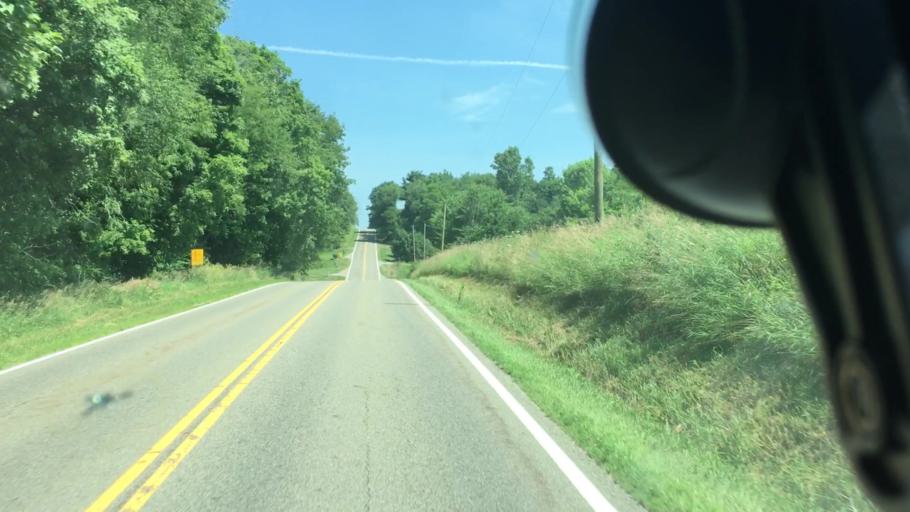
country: US
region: Ohio
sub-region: Columbiana County
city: Salem
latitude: 40.8218
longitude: -80.8581
